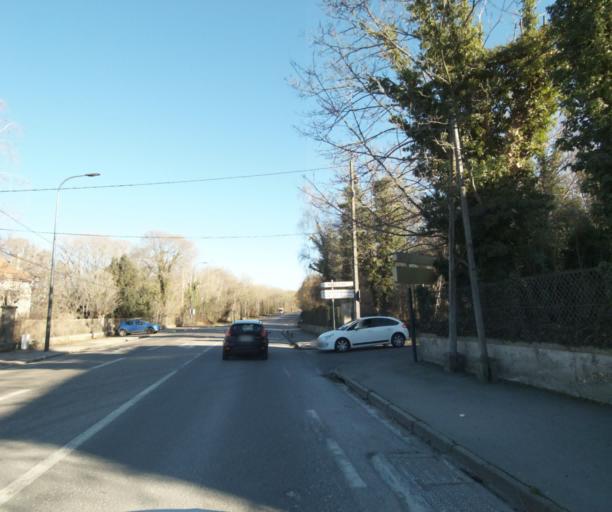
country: FR
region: Lorraine
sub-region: Departement de Meurthe-et-Moselle
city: Art-sur-Meurthe
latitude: 48.6402
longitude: 6.2708
